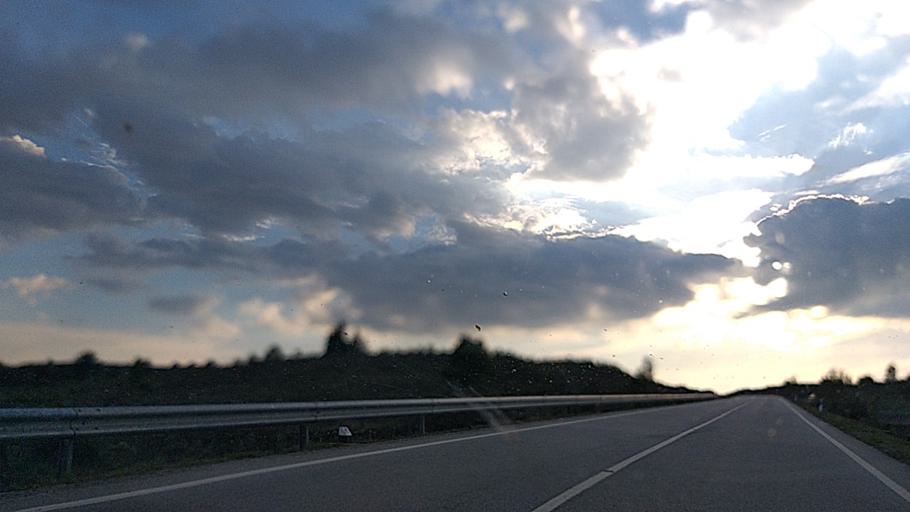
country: PT
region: Guarda
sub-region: Pinhel
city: Pinhel
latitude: 40.6870
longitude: -6.9447
